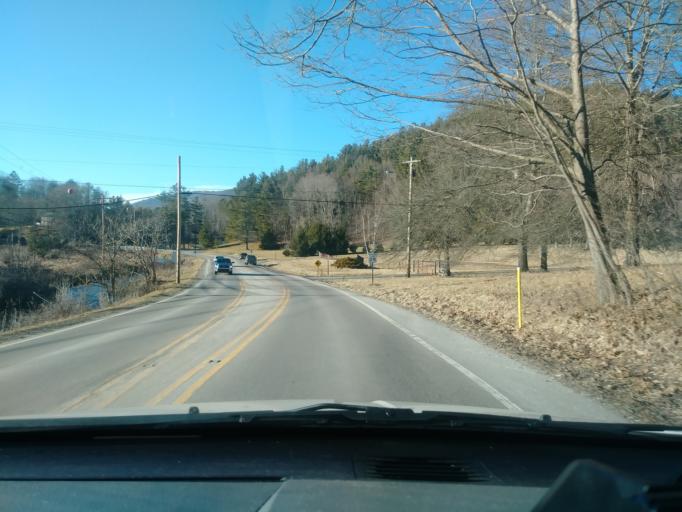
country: US
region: North Carolina
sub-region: Avery County
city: Banner Elk
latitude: 36.1551
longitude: -81.8676
